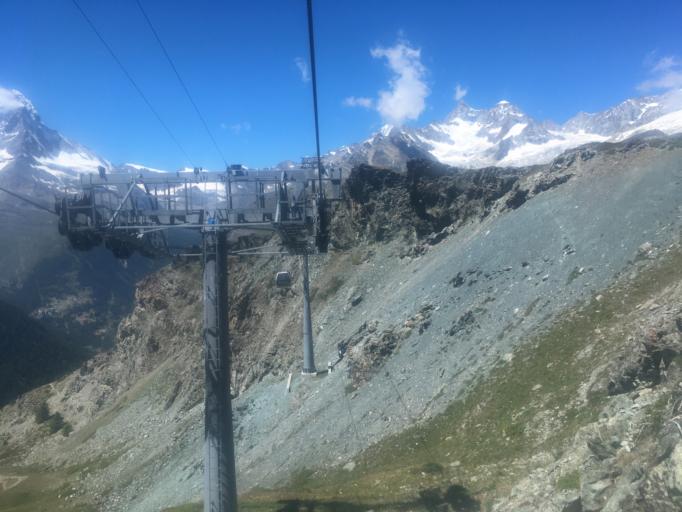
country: CH
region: Valais
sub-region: Visp District
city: Zermatt
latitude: 46.0171
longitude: 7.7827
